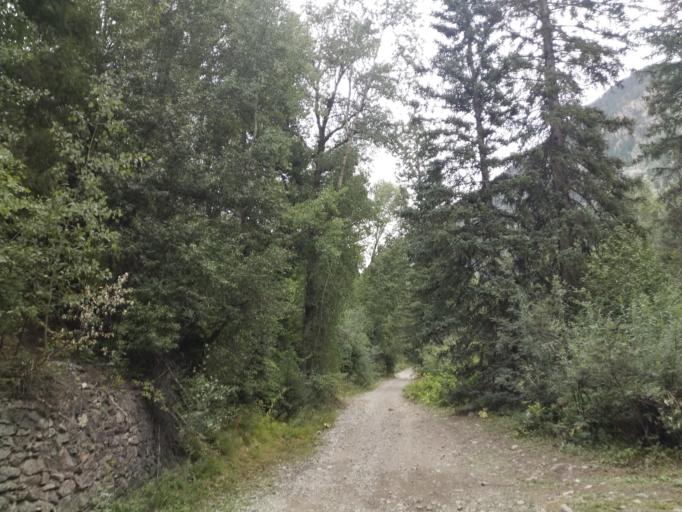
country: US
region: Colorado
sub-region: Gunnison County
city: Crested Butte
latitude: 39.0551
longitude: -107.1263
